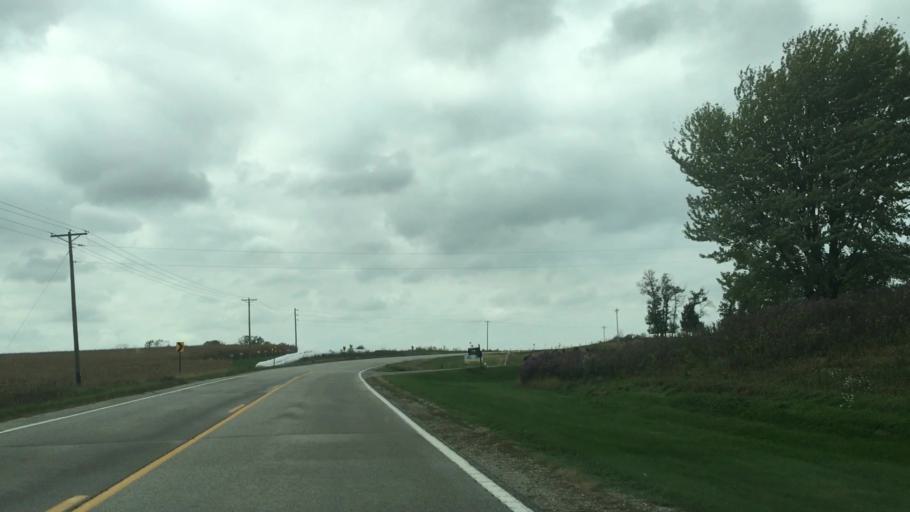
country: US
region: Minnesota
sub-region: Fillmore County
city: Preston
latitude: 43.7318
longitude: -92.0915
